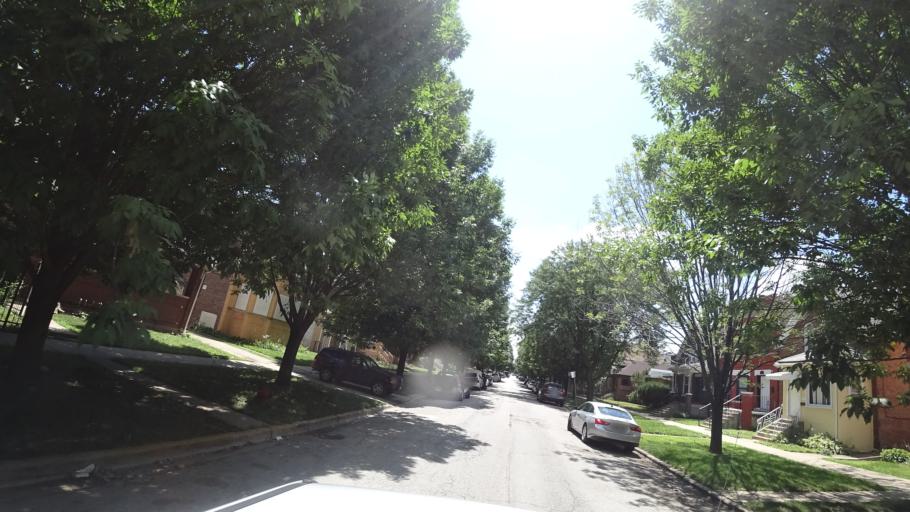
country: US
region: Illinois
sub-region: Cook County
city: Chicago
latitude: 41.7721
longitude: -87.6203
